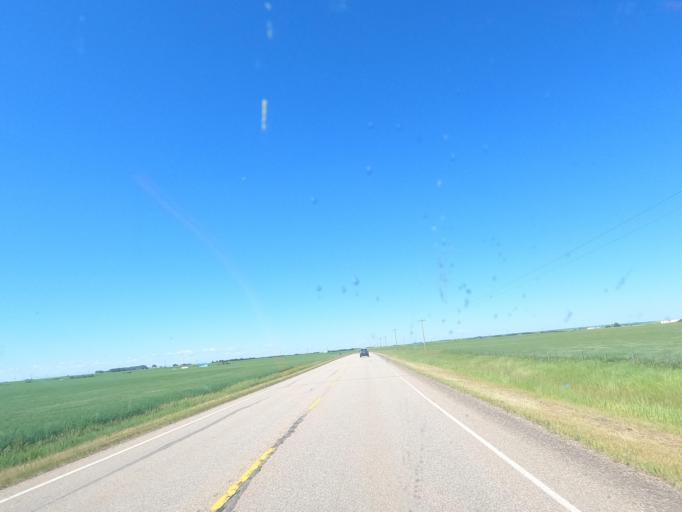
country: CA
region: Alberta
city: Irricana
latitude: 51.1543
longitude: -113.6504
